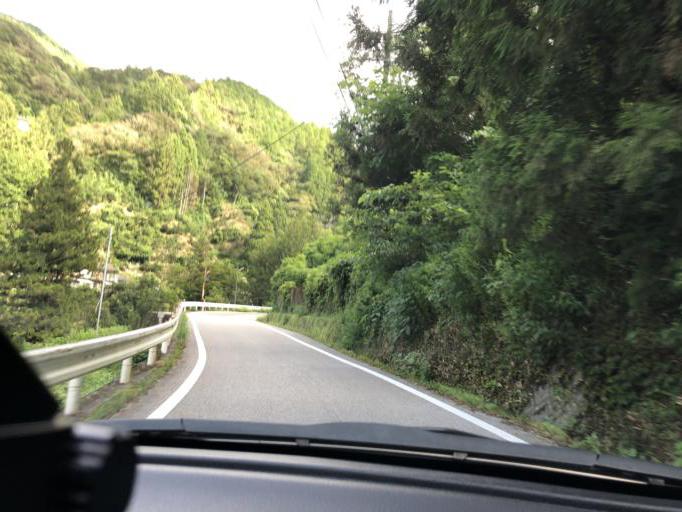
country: JP
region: Kochi
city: Kochi-shi
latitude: 33.6181
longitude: 133.4962
